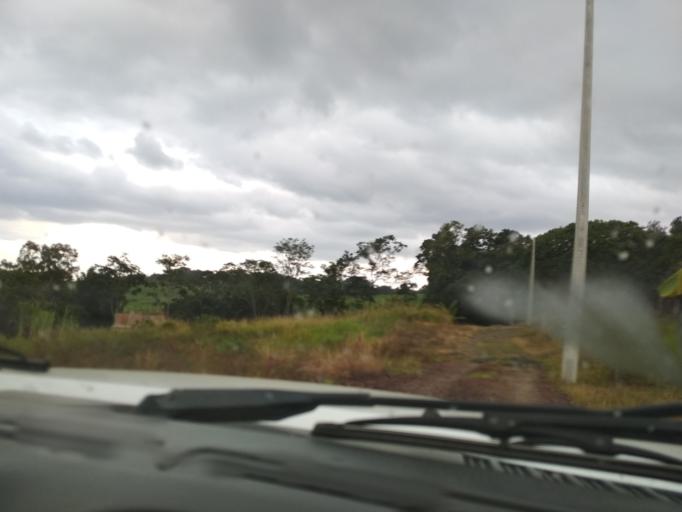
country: MX
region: Veracruz
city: El Castillo
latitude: 19.5707
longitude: -96.8308
